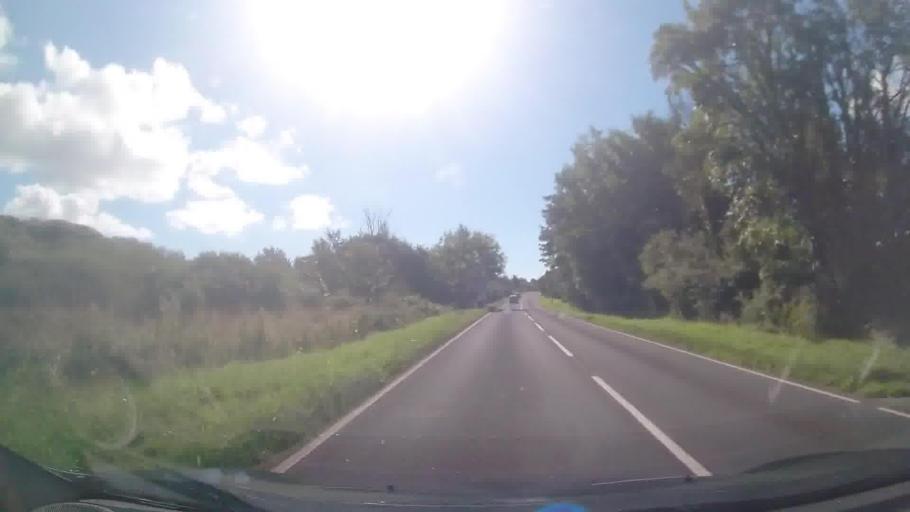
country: GB
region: Wales
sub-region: Pembrokeshire
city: Kilgetty
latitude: 51.7280
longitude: -4.7205
